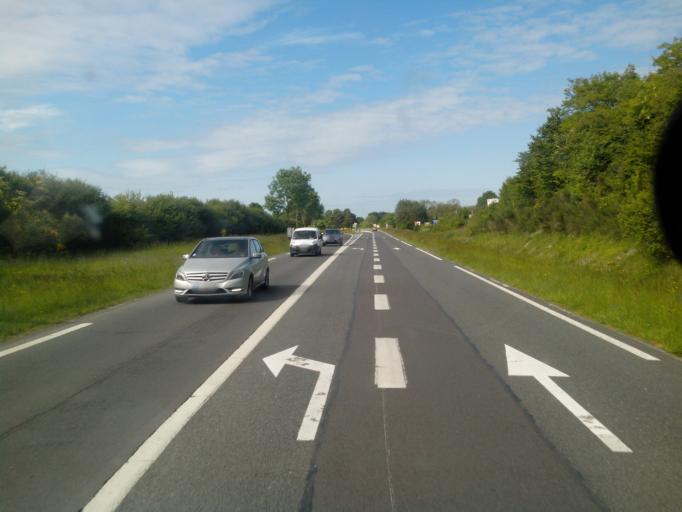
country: FR
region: Lower Normandy
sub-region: Departement du Calvados
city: Dives-sur-Mer
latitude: 49.2677
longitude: -0.1040
